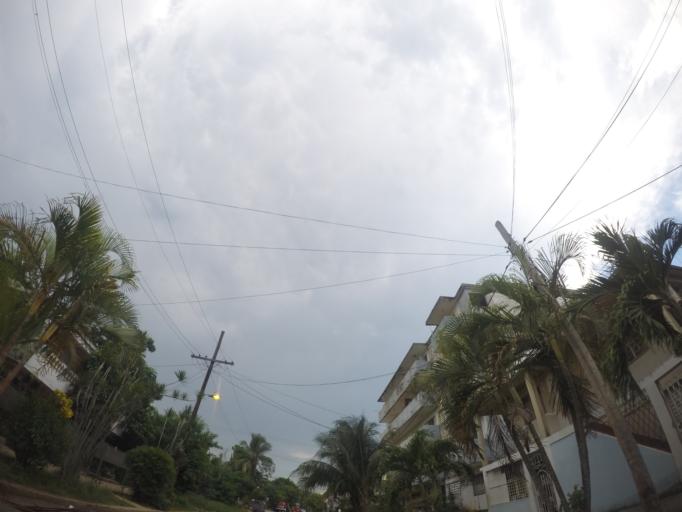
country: CU
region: La Habana
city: Havana
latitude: 23.1176
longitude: -82.4185
